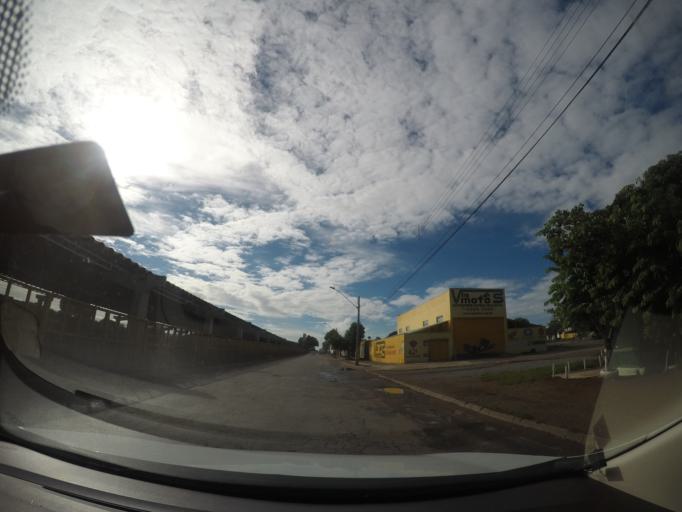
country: BR
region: Goias
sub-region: Goiania
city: Goiania
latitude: -16.6658
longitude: -49.2131
